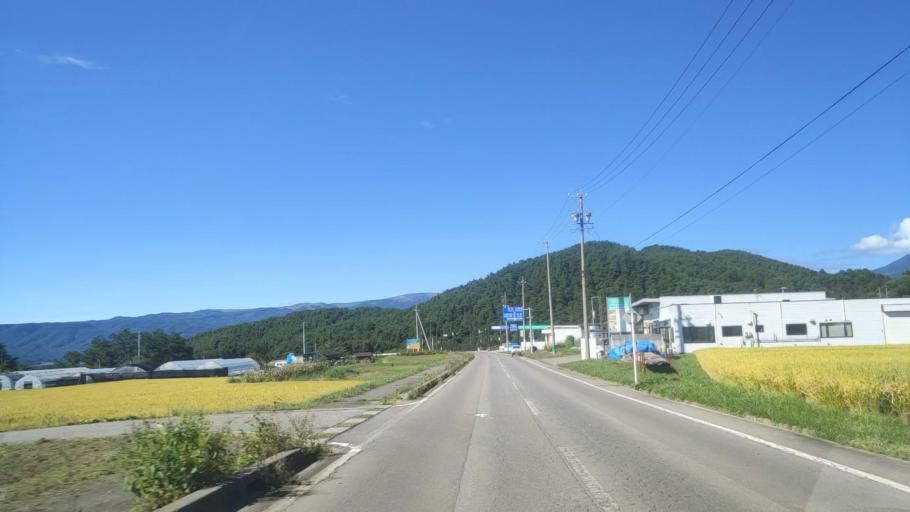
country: JP
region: Nagano
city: Chino
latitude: 35.9907
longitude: 138.2160
